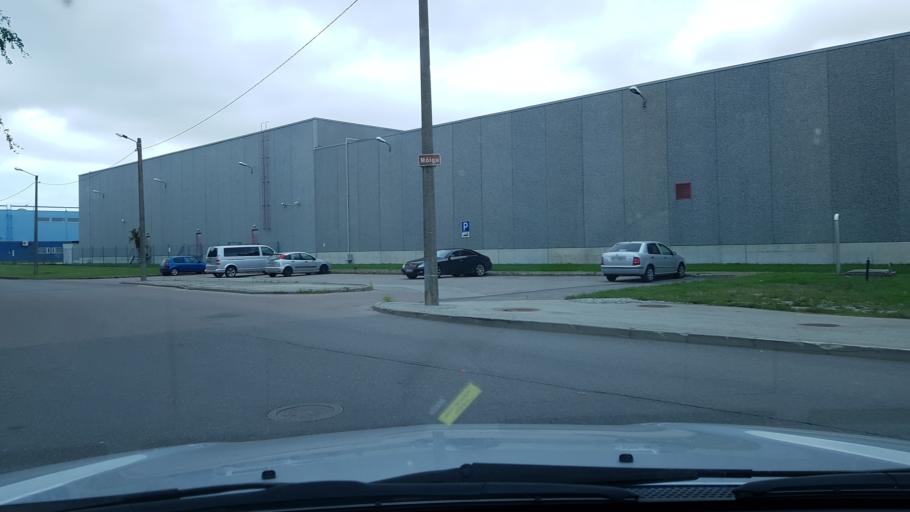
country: EE
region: Harju
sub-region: Tallinna linn
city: Tallinn
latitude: 59.4068
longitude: 24.8161
